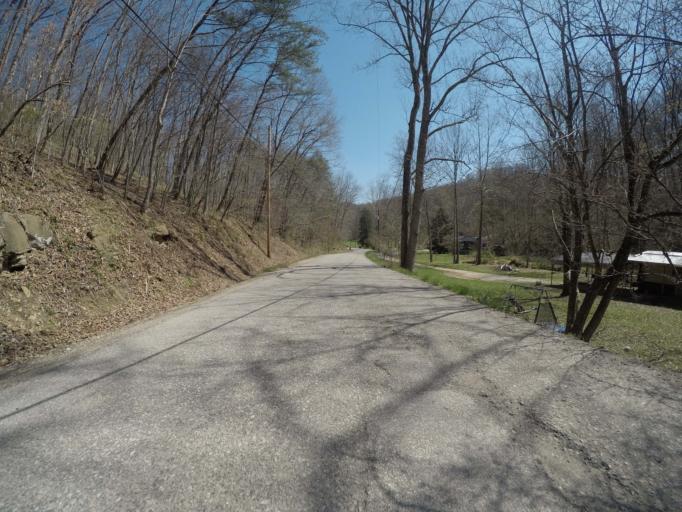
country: US
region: West Virginia
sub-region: Kanawha County
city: Charleston
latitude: 38.4154
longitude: -81.5768
